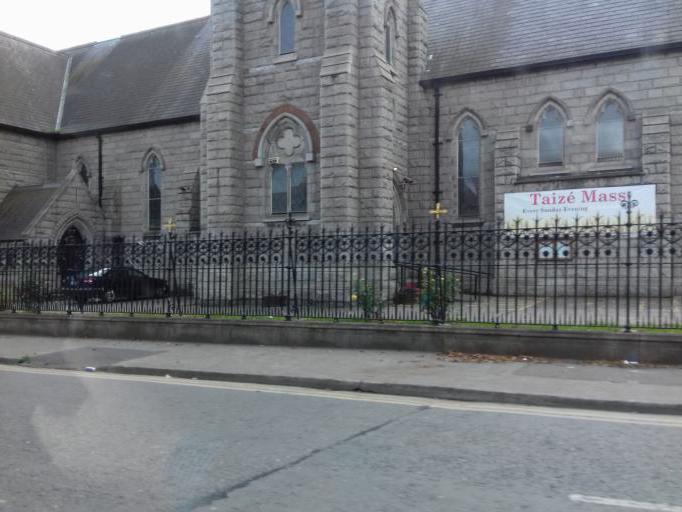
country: IE
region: Leinster
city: Rialto
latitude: 53.3331
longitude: -6.2908
